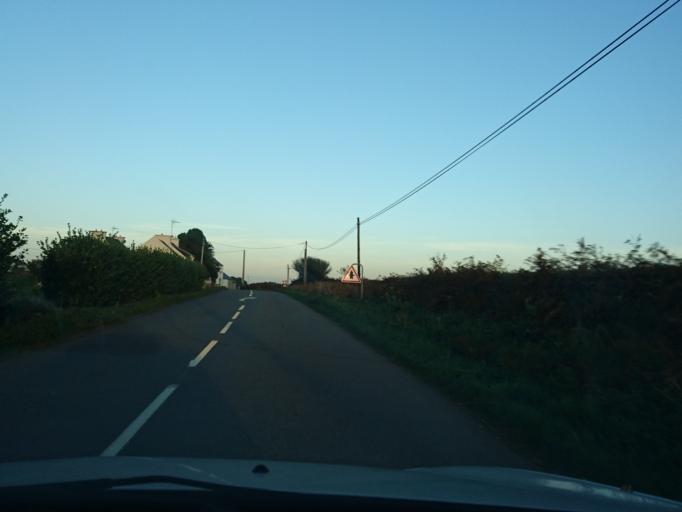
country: FR
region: Brittany
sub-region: Departement du Finistere
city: Lanrivoare
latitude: 48.4743
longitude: -4.6586
